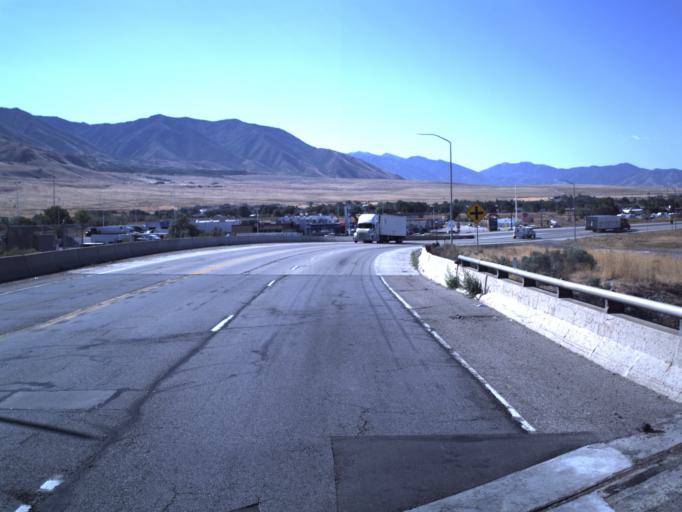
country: US
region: Utah
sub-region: Tooele County
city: Stansbury park
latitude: 40.6931
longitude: -112.2638
